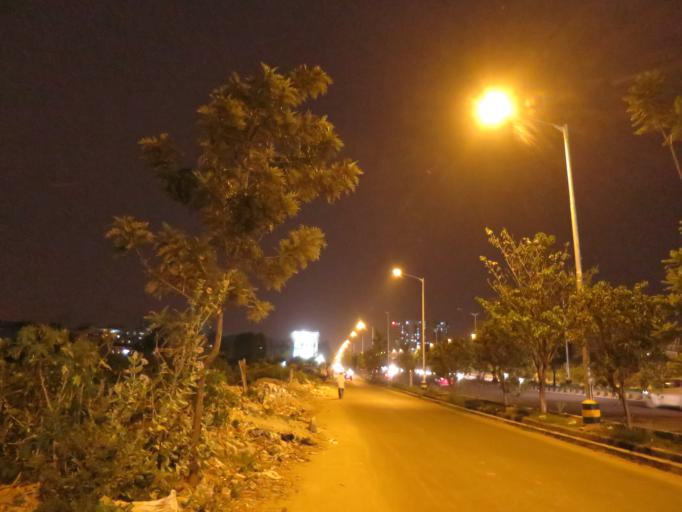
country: IN
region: Karnataka
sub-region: Bangalore Urban
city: Bangalore
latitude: 12.9841
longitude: 77.6917
